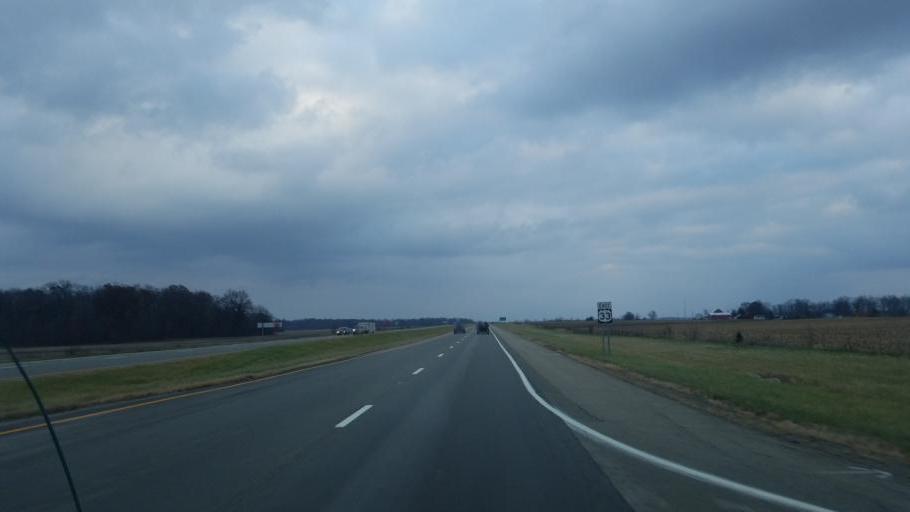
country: US
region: Ohio
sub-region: Auglaize County
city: Wapakoneta
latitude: 40.5643
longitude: -84.2598
